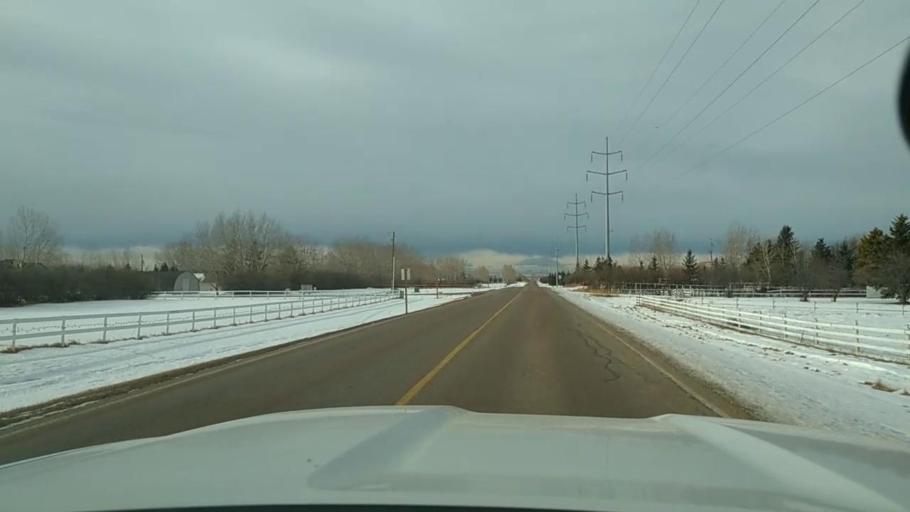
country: CA
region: Alberta
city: Airdrie
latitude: 51.2417
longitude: -113.9713
